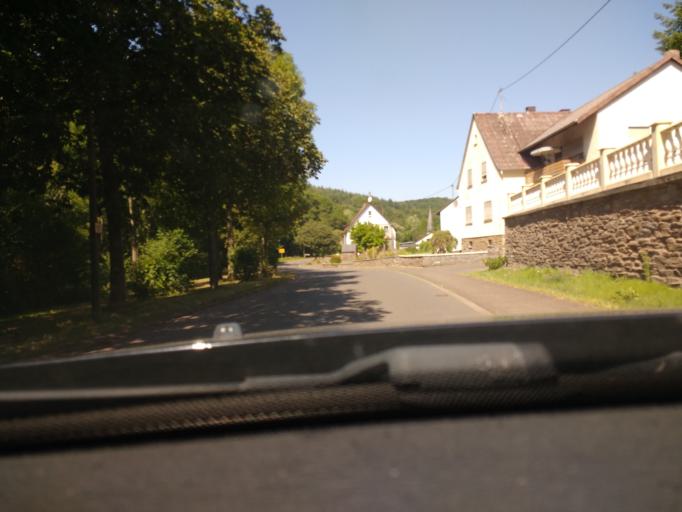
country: DE
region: Rheinland-Pfalz
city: Bausendorf
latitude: 50.0220
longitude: 6.9784
